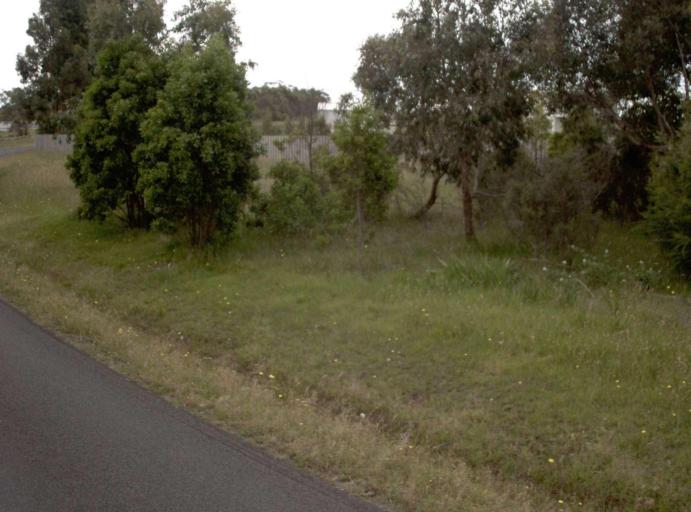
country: AU
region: Victoria
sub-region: Bass Coast
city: Cowes
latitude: -38.4228
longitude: 145.4378
